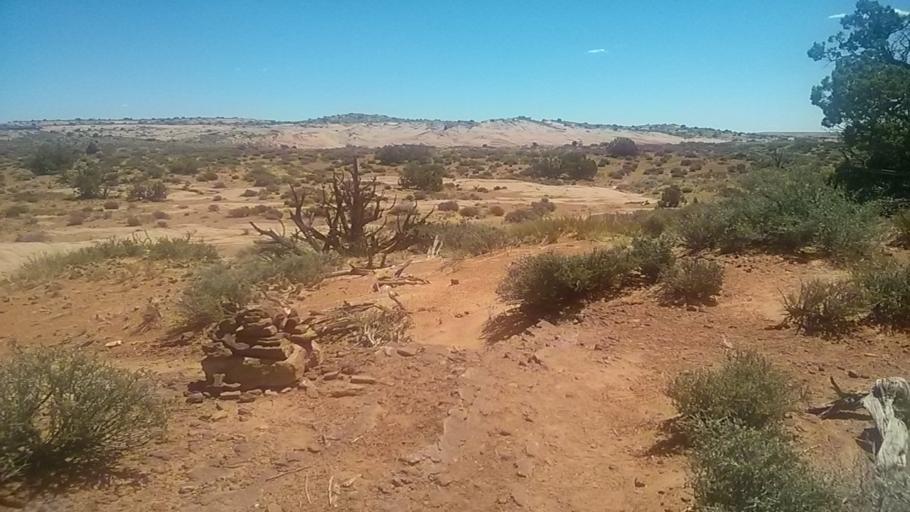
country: US
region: Arizona
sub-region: Coconino County
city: Page
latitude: 37.4850
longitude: -111.2127
